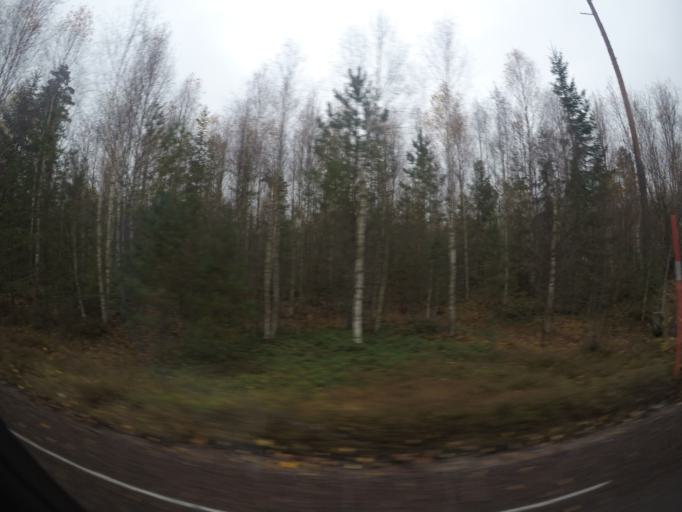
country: SE
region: Vaestmanland
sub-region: Surahammars Kommun
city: Surahammar
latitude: 59.6553
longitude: 16.0738
